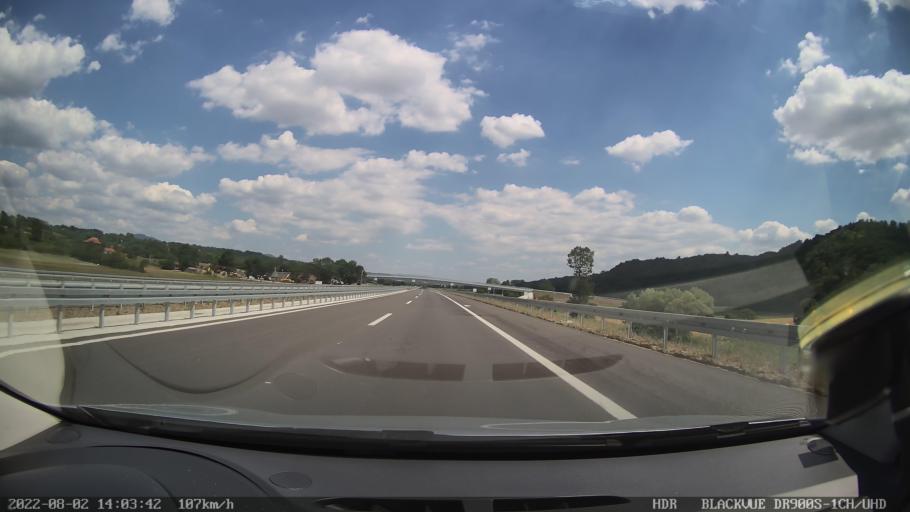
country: RS
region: Central Serbia
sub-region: Moravicki Okrug
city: Cacak
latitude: 43.9248
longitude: 20.3553
